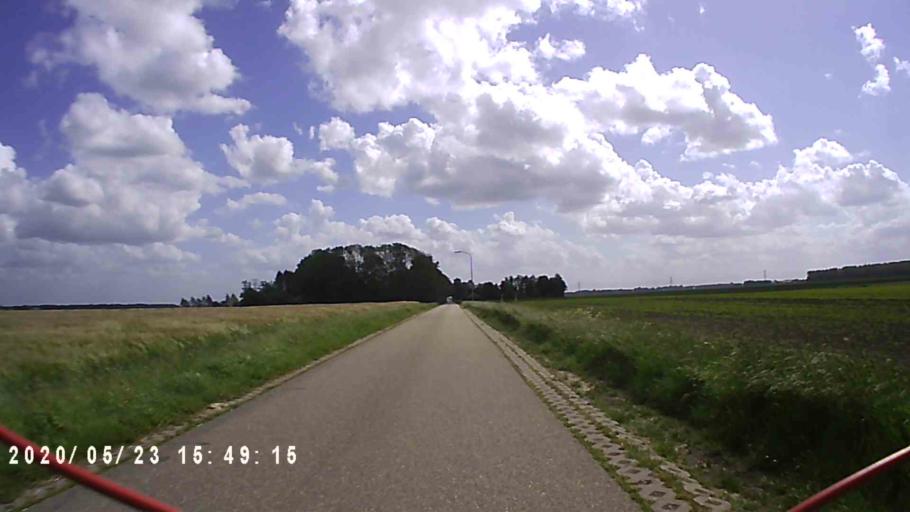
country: NL
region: Groningen
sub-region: Gemeente Delfzijl
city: Delfzijl
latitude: 53.2783
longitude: 6.9056
